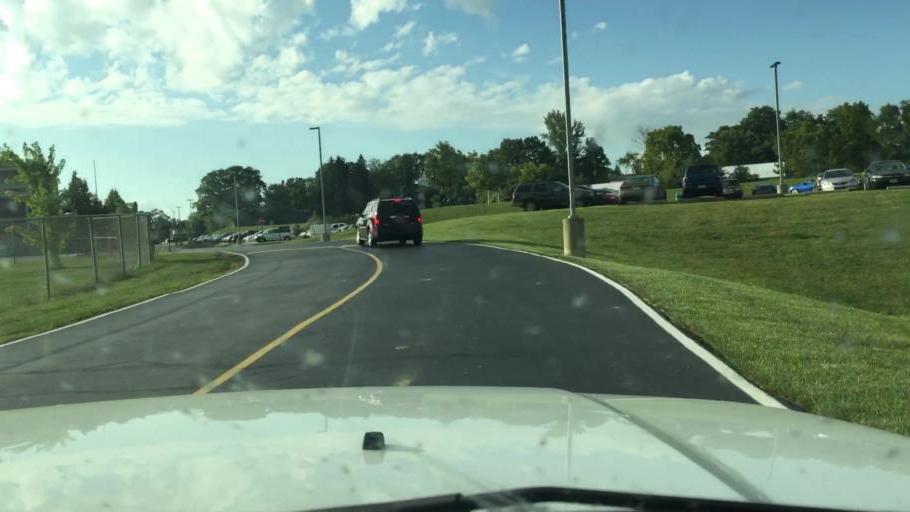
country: US
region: Ohio
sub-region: Champaign County
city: Mechanicsburg
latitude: 40.0780
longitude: -83.5611
